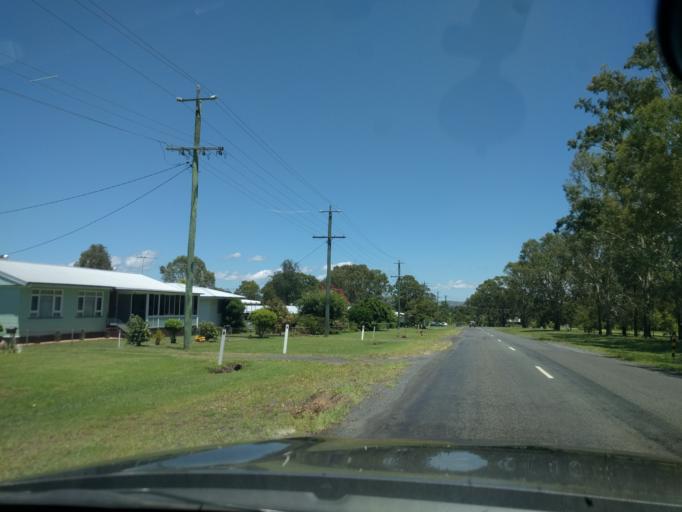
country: AU
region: Queensland
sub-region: Logan
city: Cedar Vale
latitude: -27.9980
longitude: 153.0002
